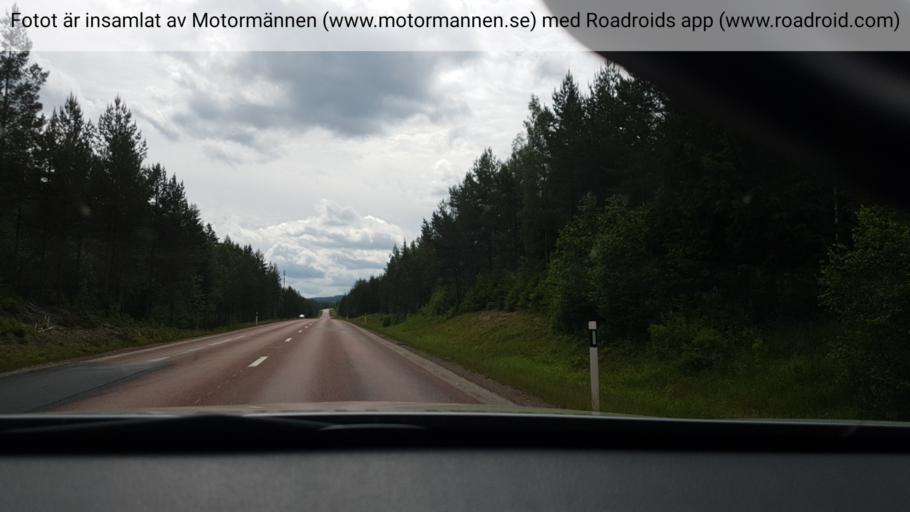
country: SE
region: Vaermland
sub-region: Hagfors Kommun
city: Ekshaerad
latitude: 60.4092
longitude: 13.2562
